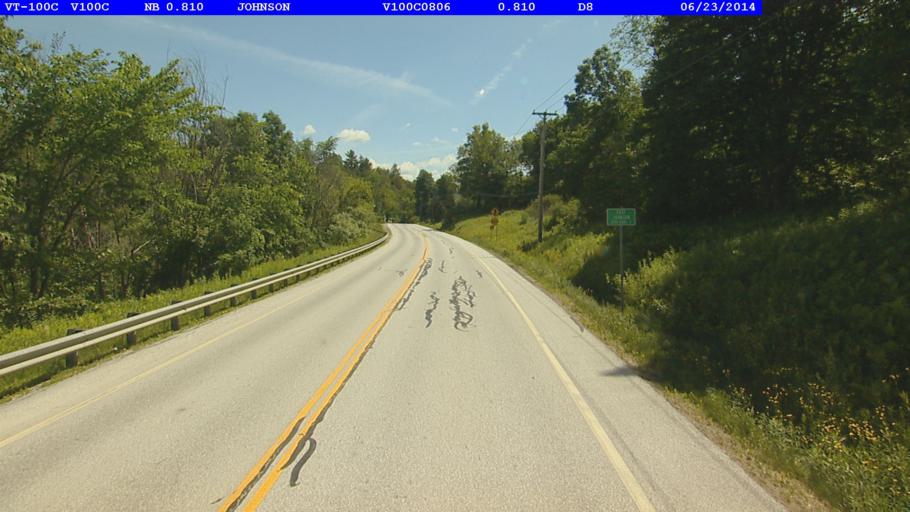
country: US
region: Vermont
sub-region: Lamoille County
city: Johnson
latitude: 44.6397
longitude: -72.6637
